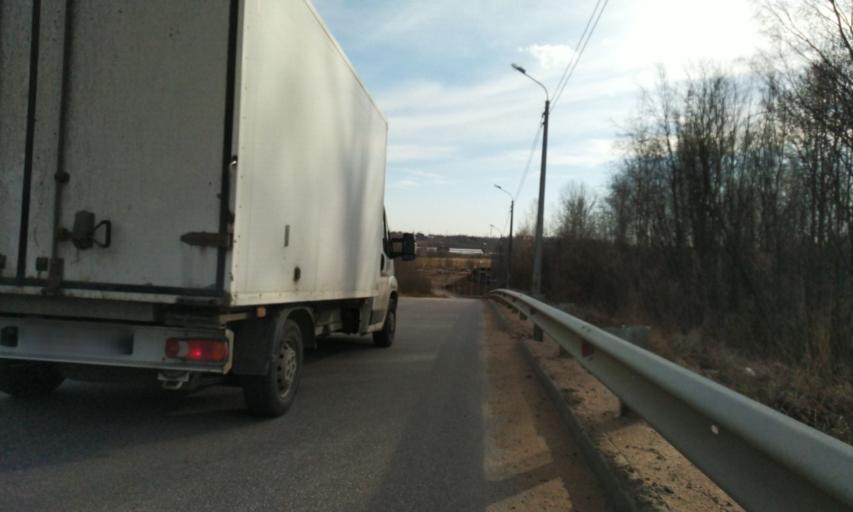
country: RU
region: Leningrad
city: Bugry
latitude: 60.1174
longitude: 30.4272
